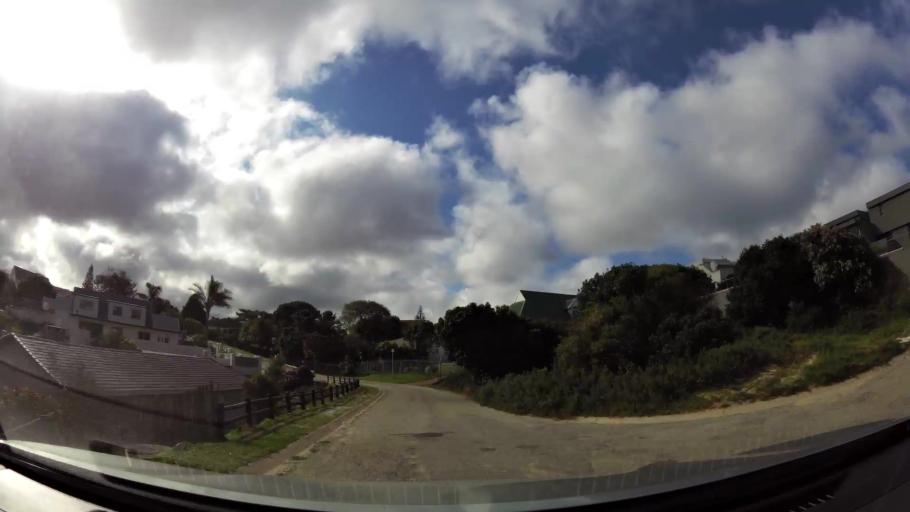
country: ZA
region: Western Cape
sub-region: Eden District Municipality
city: Plettenberg Bay
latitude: -34.0704
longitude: 23.3722
